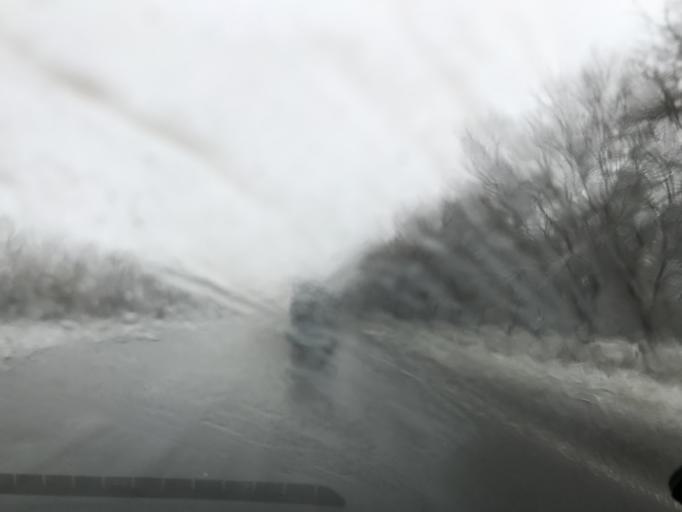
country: RU
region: Rostov
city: Yegorlykskaya
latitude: 46.6053
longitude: 40.6132
